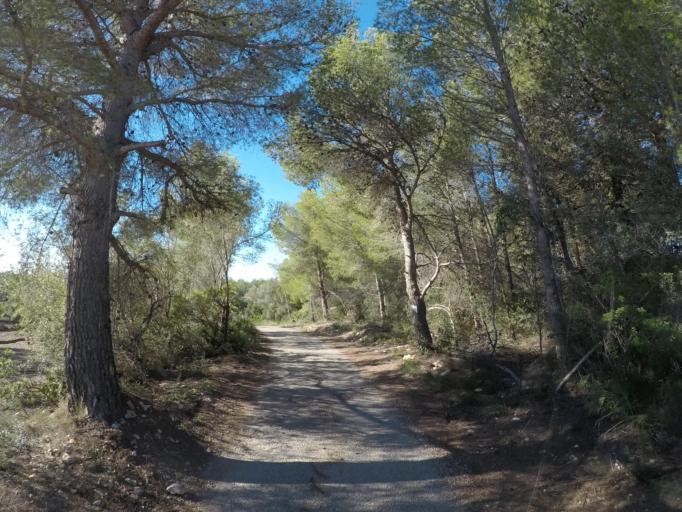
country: ES
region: Catalonia
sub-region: Provincia de Tarragona
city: El Perello
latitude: 40.9155
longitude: 0.7232
